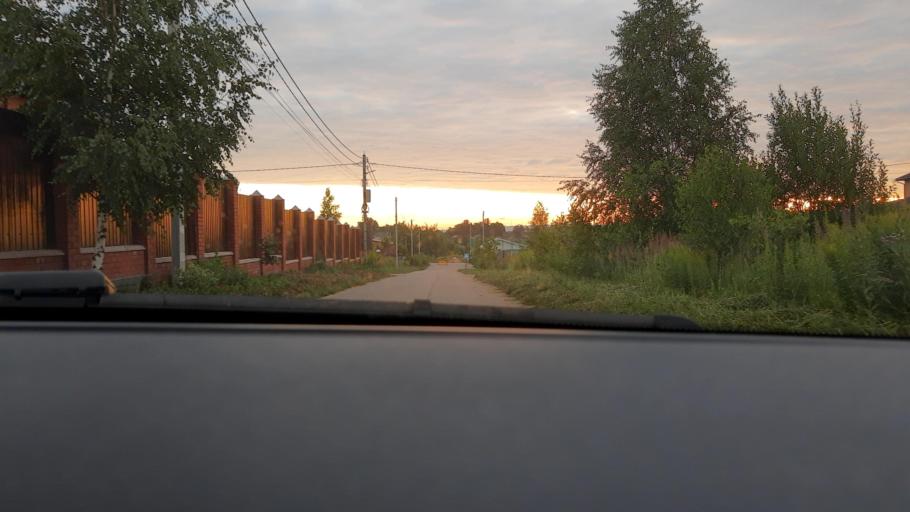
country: RU
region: Nizjnij Novgorod
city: Burevestnik
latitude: 56.1947
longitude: 43.8652
